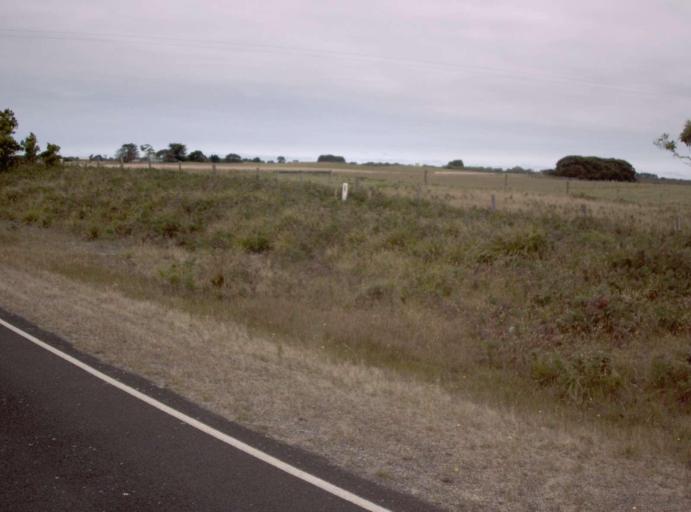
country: AU
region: Victoria
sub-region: Wellington
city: Sale
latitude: -38.5451
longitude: 146.9523
